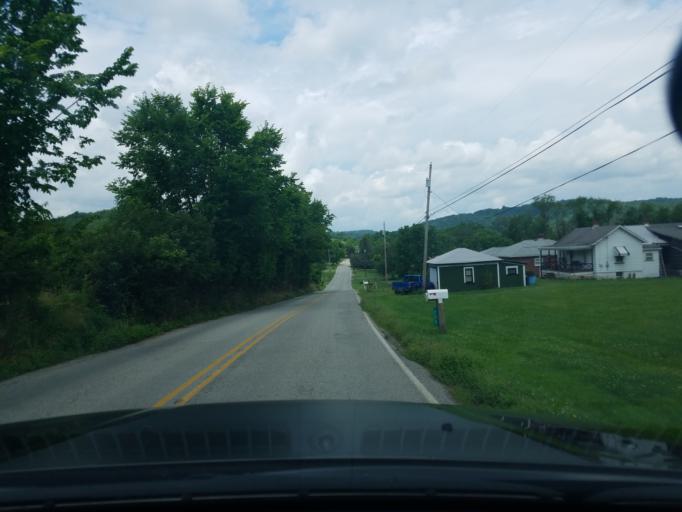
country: US
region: Pennsylvania
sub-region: Westmoreland County
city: Youngwood
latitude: 40.2108
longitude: -79.5373
